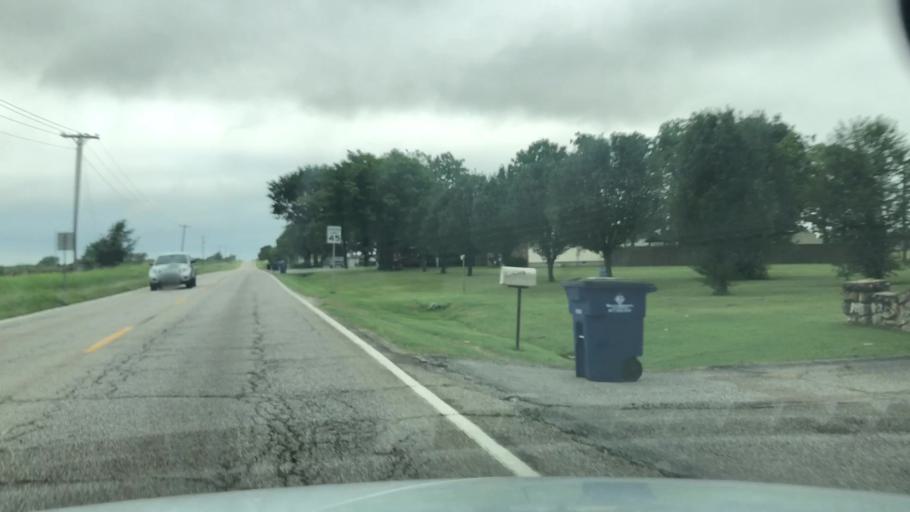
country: US
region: Oklahoma
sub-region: Nowata County
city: Nowata
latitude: 36.7056
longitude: -95.6522
